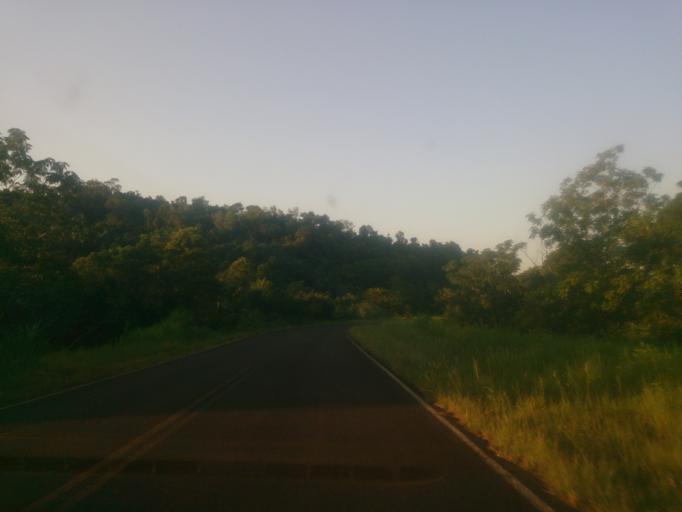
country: AR
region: Misiones
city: Panambi
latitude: -27.6995
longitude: -54.9073
